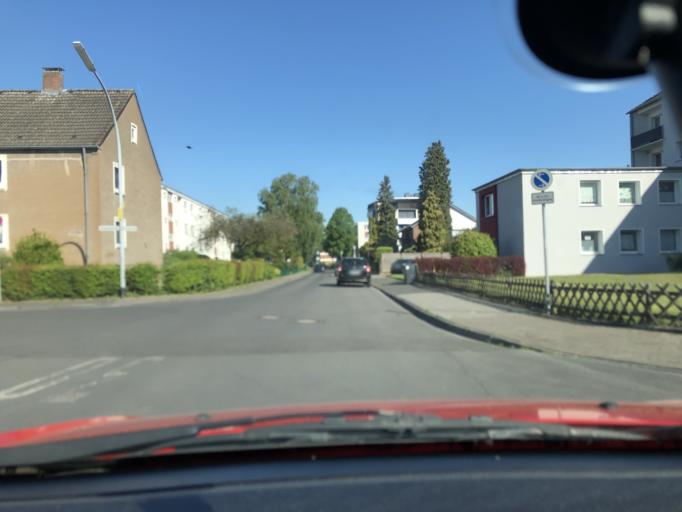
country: DE
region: North Rhine-Westphalia
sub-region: Regierungsbezirk Dusseldorf
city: Kamp-Lintfort
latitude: 51.4984
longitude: 6.5311
